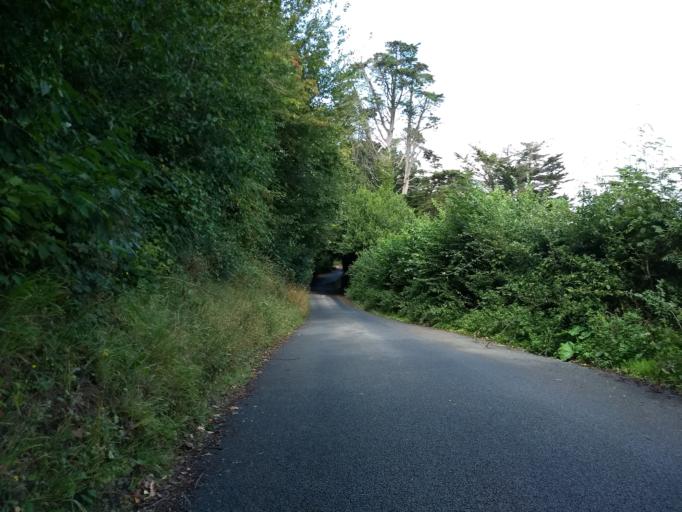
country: GB
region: England
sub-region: Isle of Wight
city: Newport
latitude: 50.6796
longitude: -1.2932
